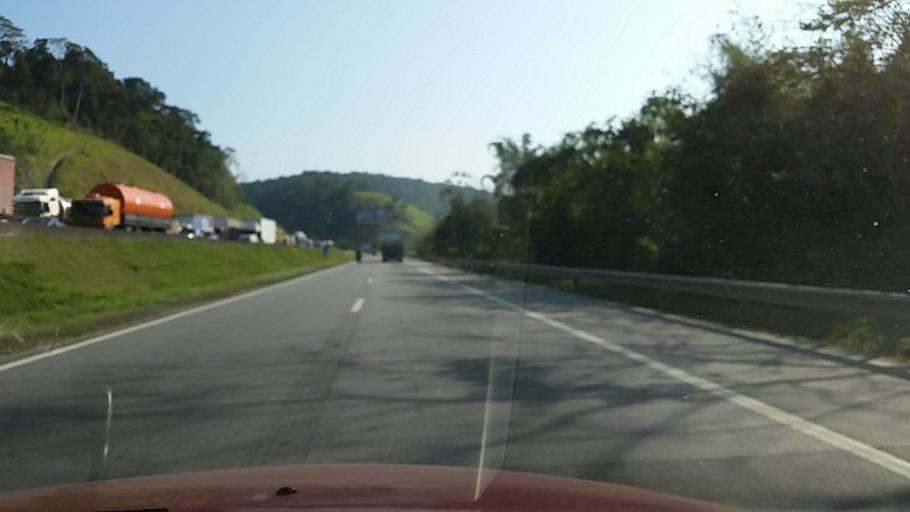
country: BR
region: Sao Paulo
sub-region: Miracatu
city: Miracatu
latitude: -24.1824
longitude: -47.3548
